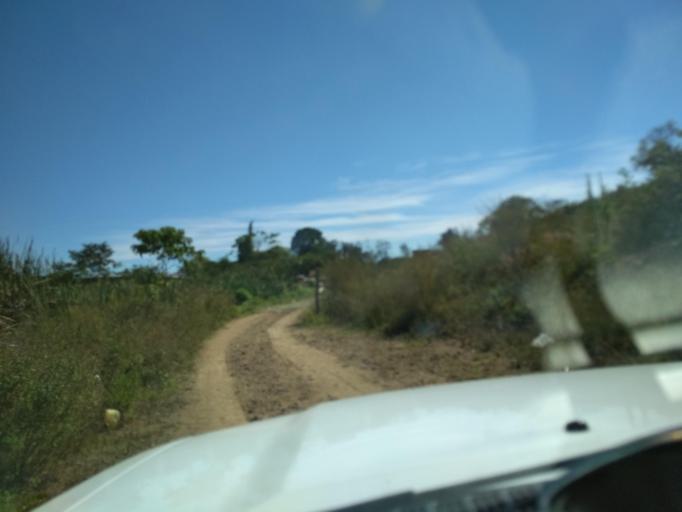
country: MX
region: Veracruz
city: El Castillo
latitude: 19.5471
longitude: -96.8538
